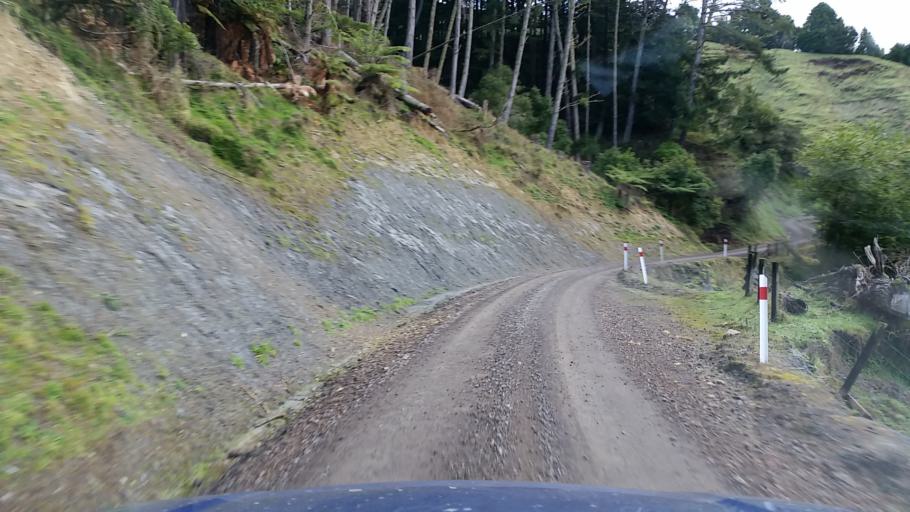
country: NZ
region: Taranaki
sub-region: New Plymouth District
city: Waitara
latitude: -39.0967
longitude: 174.8386
